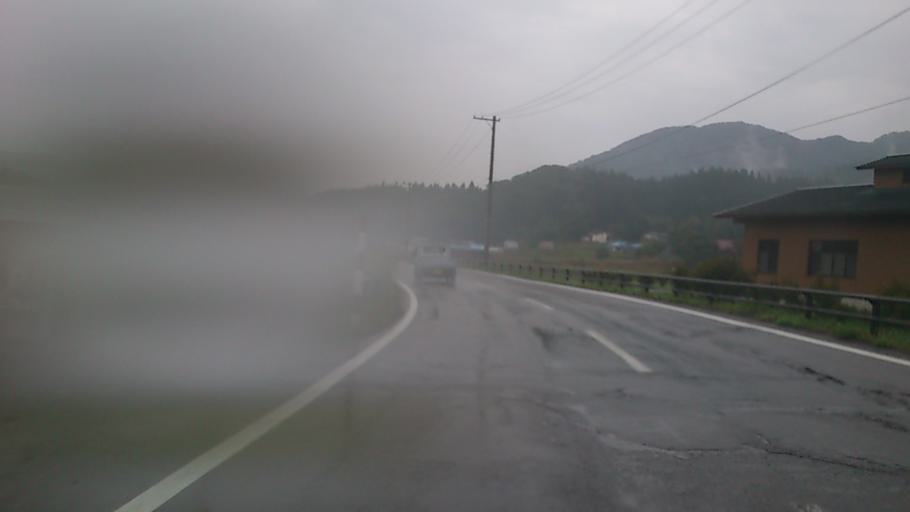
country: JP
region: Akita
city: Takanosu
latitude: 40.2980
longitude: 140.2841
